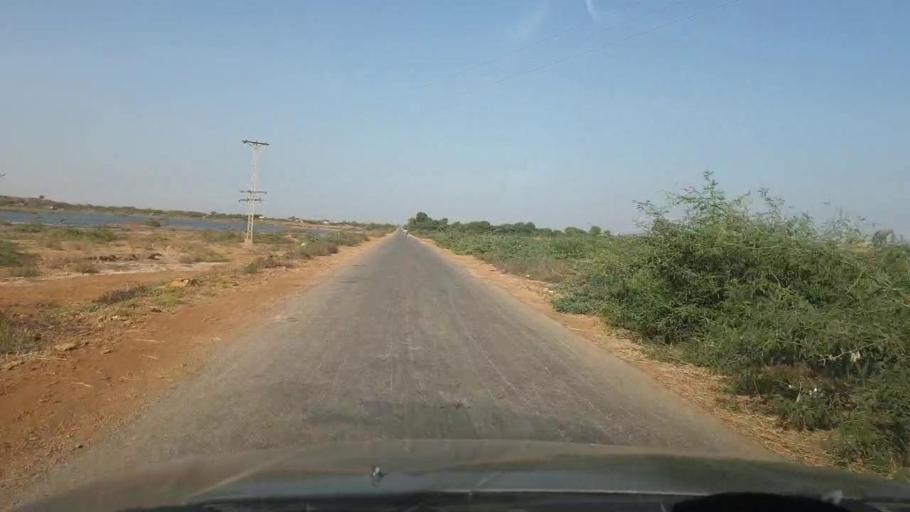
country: PK
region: Sindh
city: Bulri
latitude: 25.0920
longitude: 68.2339
